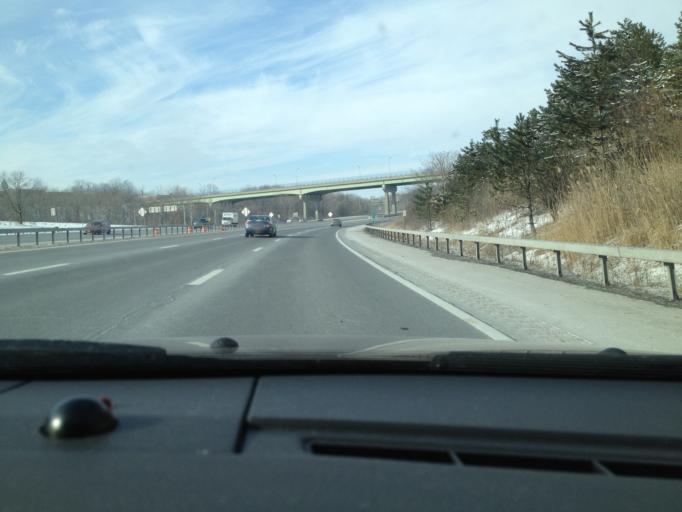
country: US
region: New York
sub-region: Albany County
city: Albany
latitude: 42.6698
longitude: -73.7501
